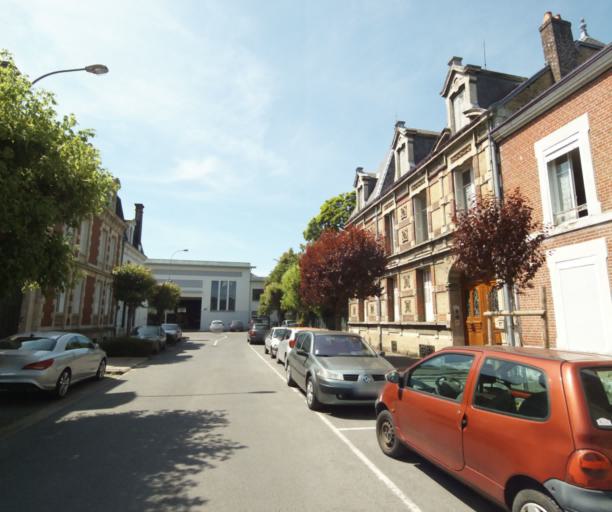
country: FR
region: Champagne-Ardenne
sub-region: Departement des Ardennes
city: Charleville-Mezieres
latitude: 49.7650
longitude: 4.7188
